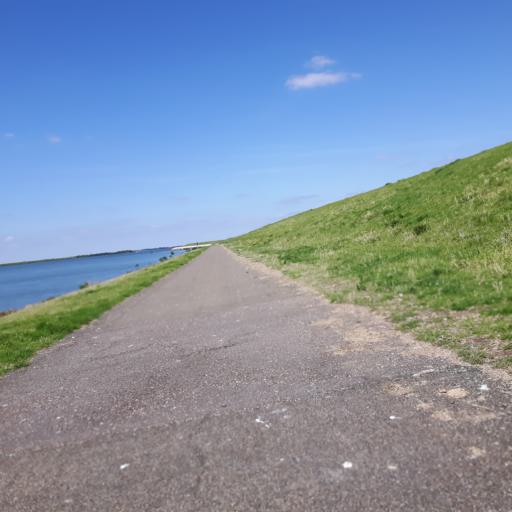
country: NL
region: Zeeland
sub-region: Gemeente Tholen
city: Tholen
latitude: 51.4671
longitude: 4.2311
